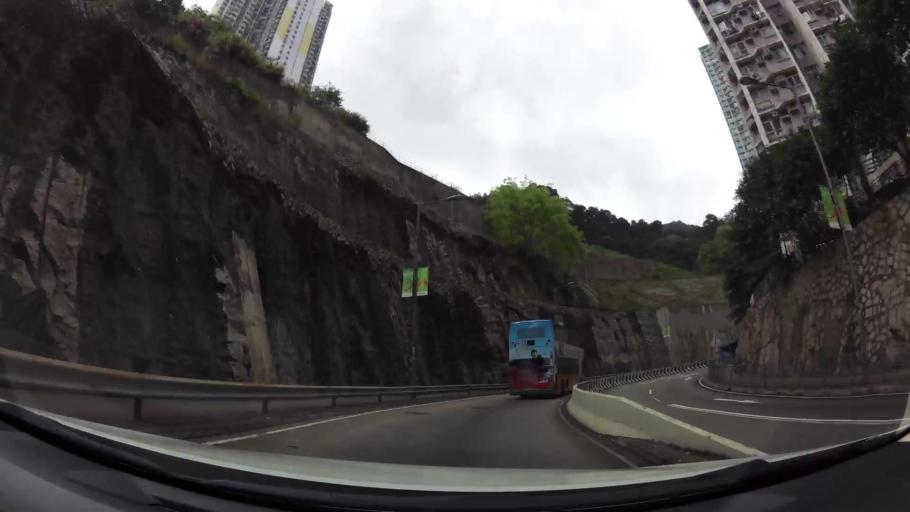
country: HK
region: Wanchai
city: Wan Chai
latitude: 22.2802
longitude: 114.2210
